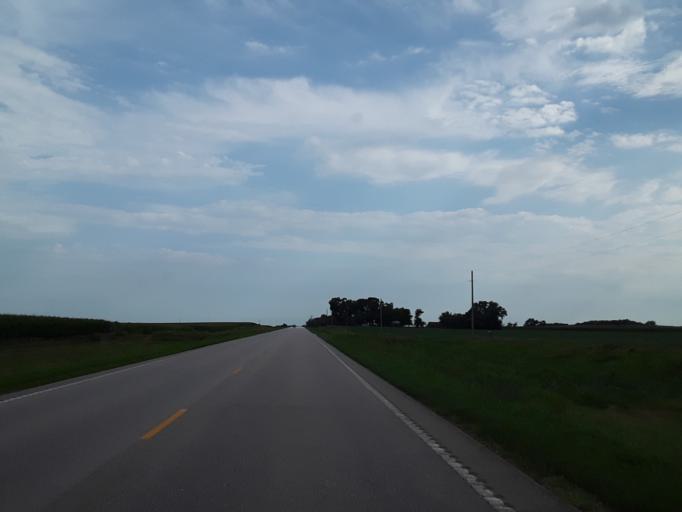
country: US
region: Nebraska
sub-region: Saunders County
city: Ashland
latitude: 41.1264
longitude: -96.4257
